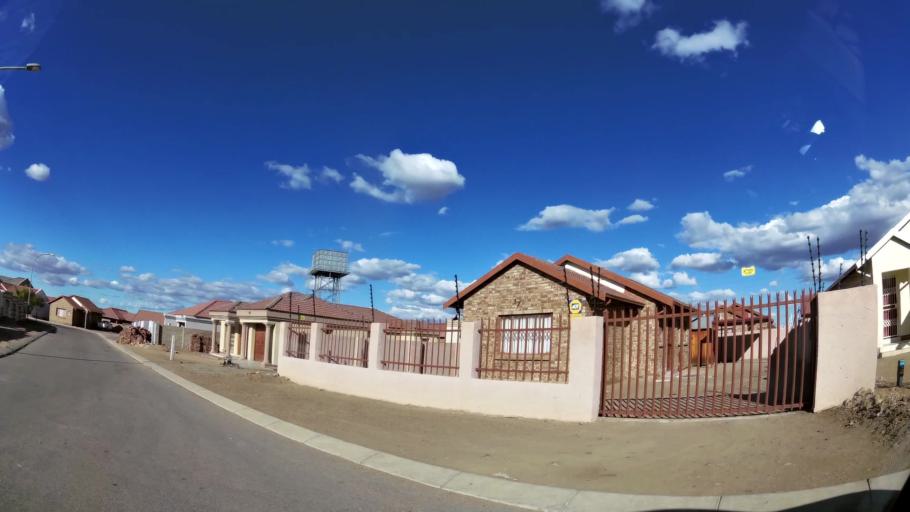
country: ZA
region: Limpopo
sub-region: Capricorn District Municipality
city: Polokwane
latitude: -23.9420
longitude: 29.4429
